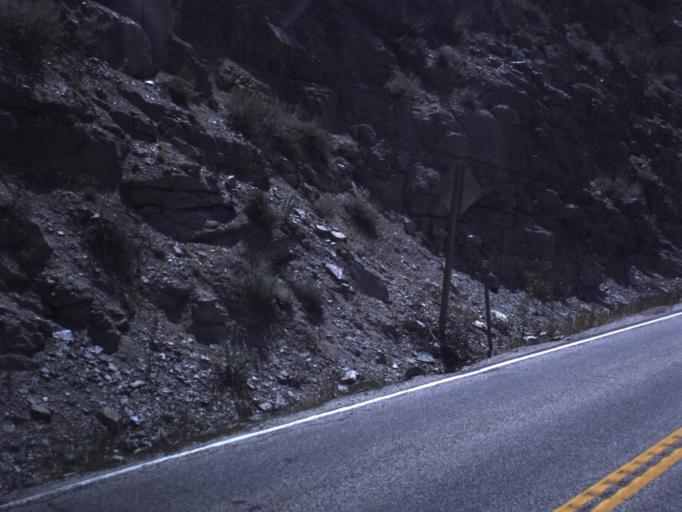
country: US
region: Utah
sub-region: Cache County
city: North Logan
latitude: 41.8250
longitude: -111.6020
